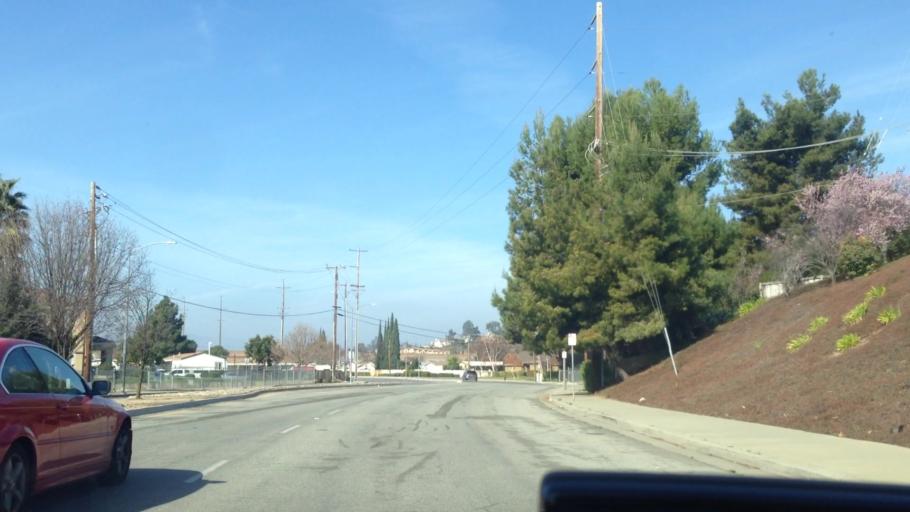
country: US
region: California
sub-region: Santa Clara County
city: Seven Trees
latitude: 37.2803
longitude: -121.8599
